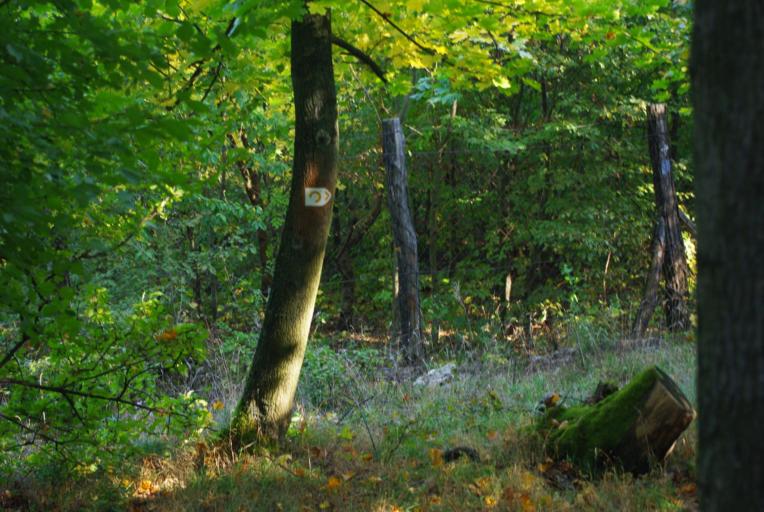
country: HU
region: Pest
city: Budakeszi
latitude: 47.5385
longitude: 18.9124
